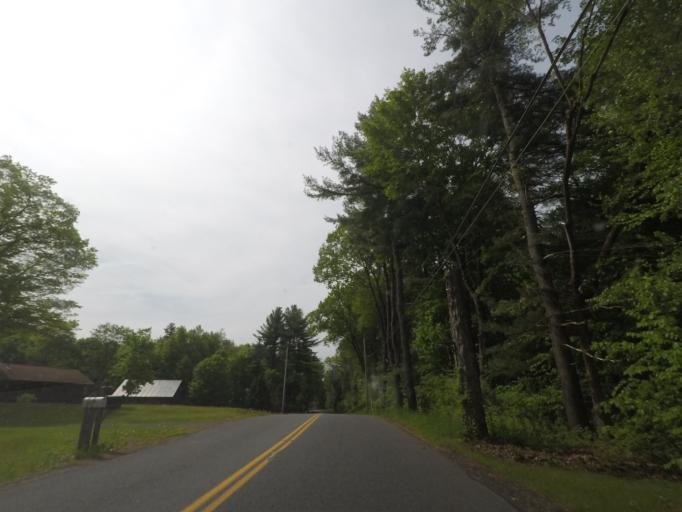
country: US
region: New York
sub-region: Saratoga County
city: Stillwater
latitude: 42.9795
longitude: -73.7155
